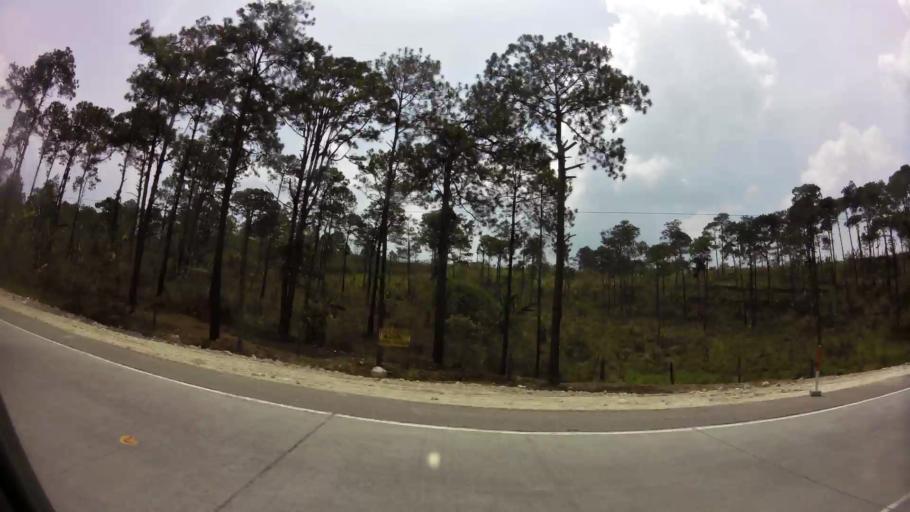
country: HN
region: Comayagua
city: El Socorro
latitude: 14.6448
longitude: -87.9262
